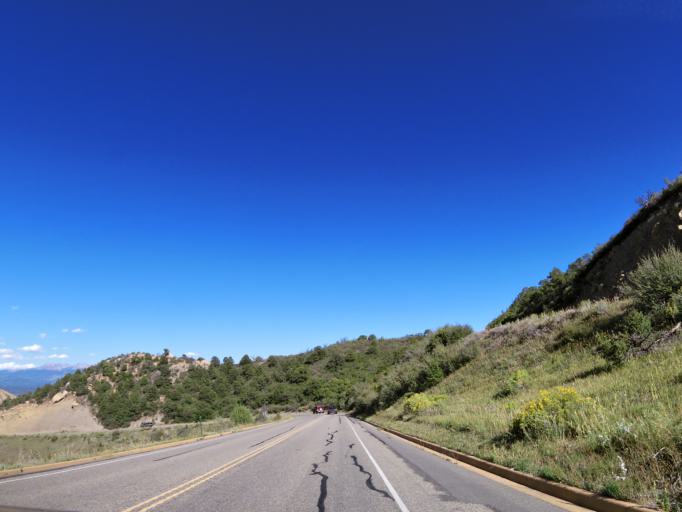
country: US
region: Colorado
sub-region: Montezuma County
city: Mancos
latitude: 37.3203
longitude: -108.4197
